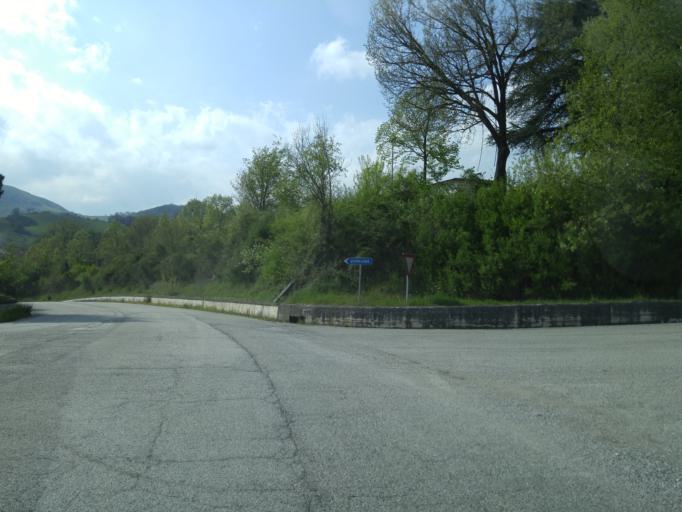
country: IT
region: The Marches
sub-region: Provincia di Pesaro e Urbino
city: Acqualagna
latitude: 43.6391
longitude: 12.6942
